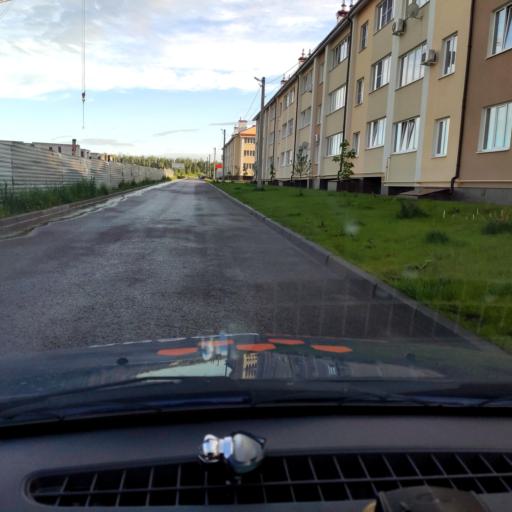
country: RU
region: Voronezj
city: Podgornoye
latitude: 51.7907
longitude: 39.1915
